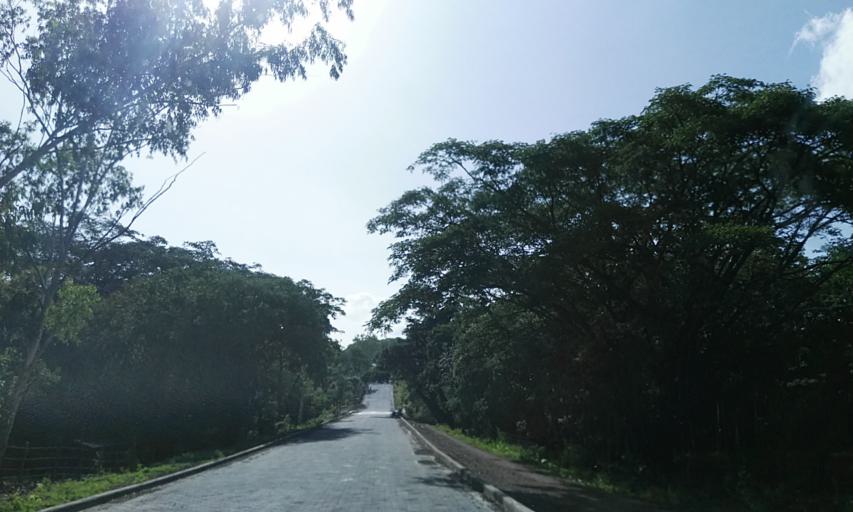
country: NI
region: Matagalpa
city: Ciudad Dario
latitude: 12.7314
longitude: -86.0732
